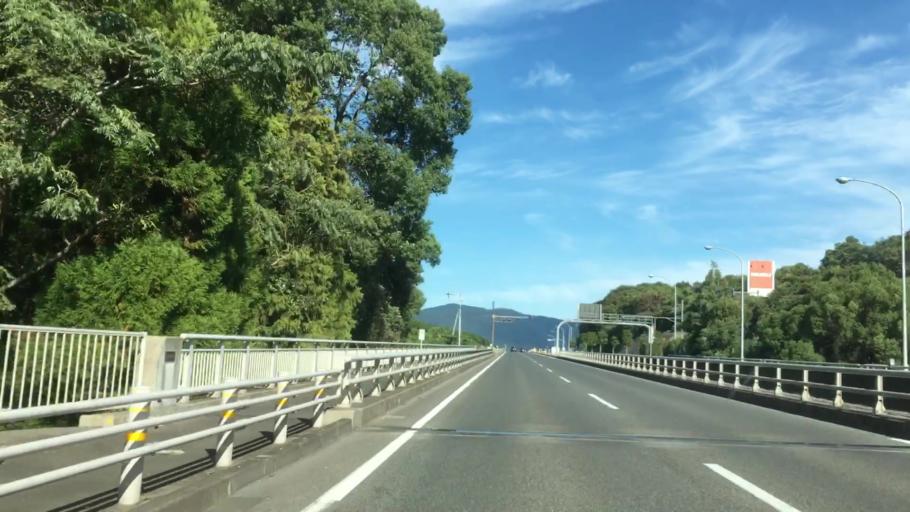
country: JP
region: Nagasaki
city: Sasebo
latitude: 33.1225
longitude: 129.7912
